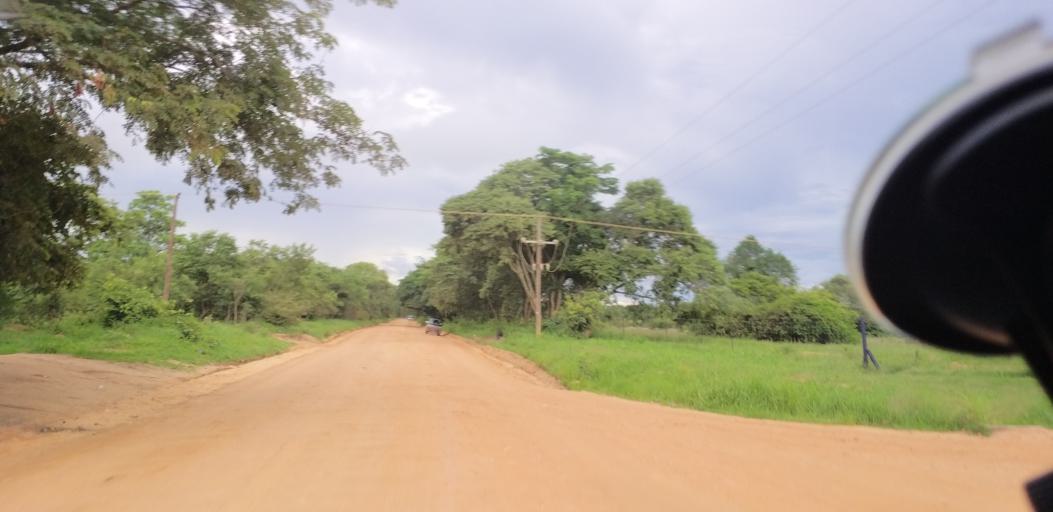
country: ZM
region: Lusaka
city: Chongwe
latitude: -15.1833
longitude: 28.4489
